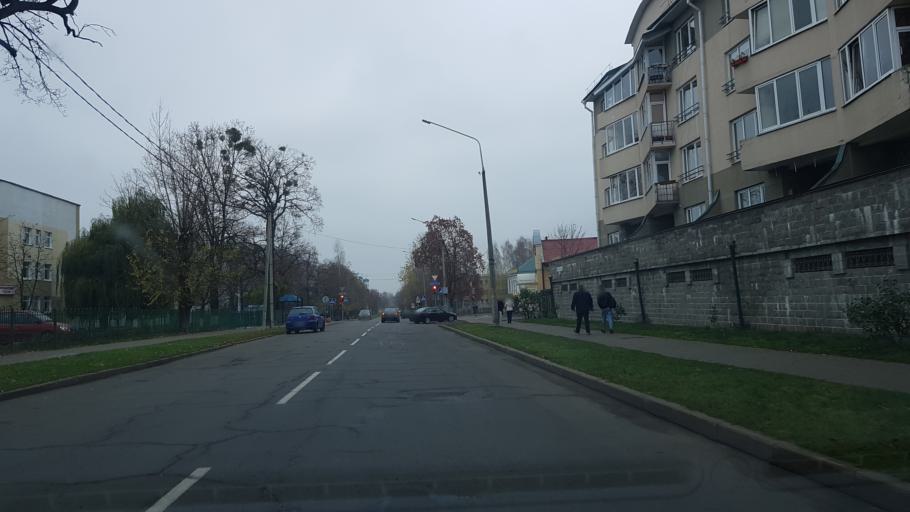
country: BY
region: Mogilev
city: Babruysk
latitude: 53.1493
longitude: 29.2373
